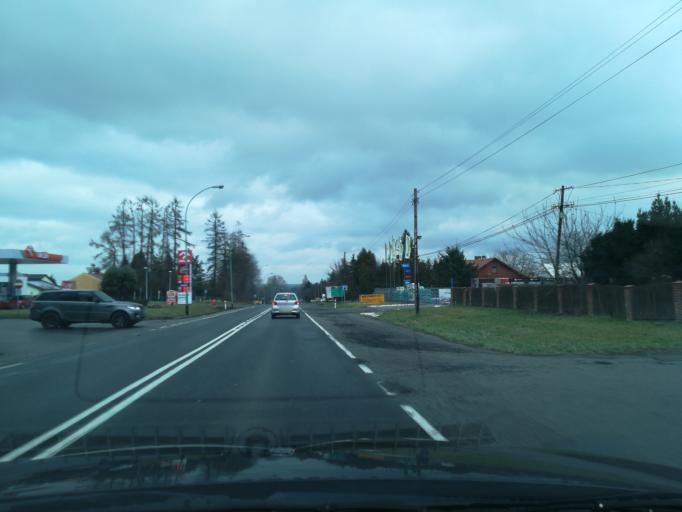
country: PL
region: Subcarpathian Voivodeship
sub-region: Powiat lancucki
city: Sonina
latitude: 50.0751
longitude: 22.2544
